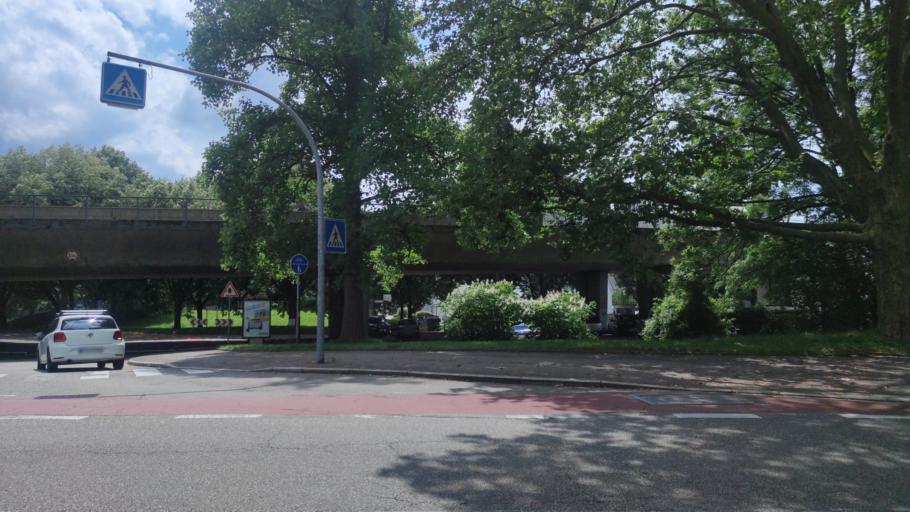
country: DE
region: Baden-Wuerttemberg
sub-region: Karlsruhe Region
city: Sinzheim
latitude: 48.7836
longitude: 8.2030
